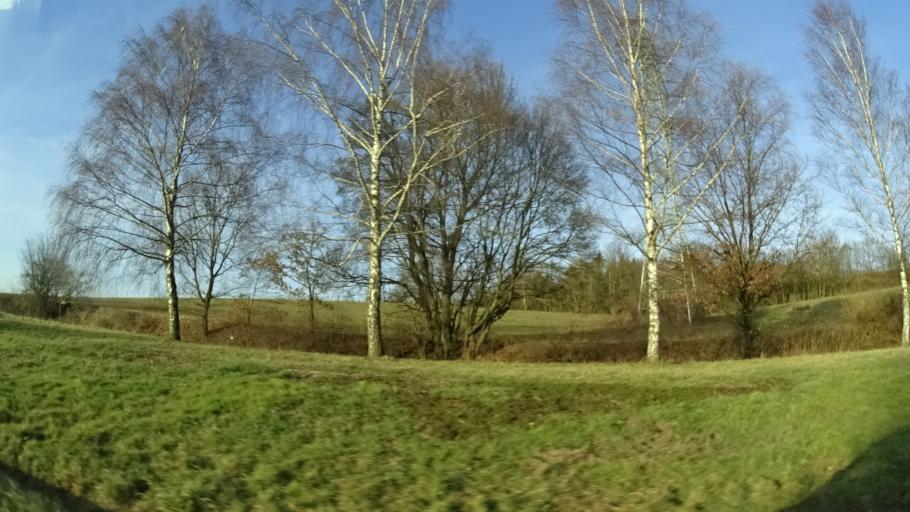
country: DE
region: Hesse
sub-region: Regierungsbezirk Darmstadt
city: Schluchtern
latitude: 50.3208
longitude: 9.5985
